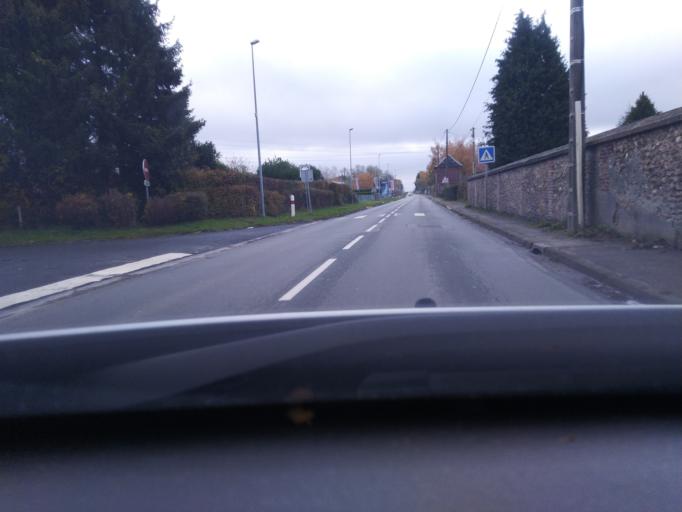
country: FR
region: Haute-Normandie
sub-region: Departement de la Seine-Maritime
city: La Vaupaliere
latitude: 49.4867
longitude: 1.0087
